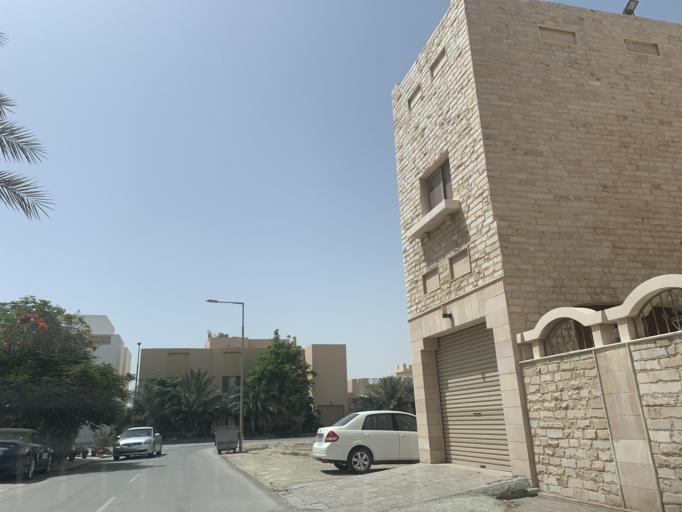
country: BH
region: Northern
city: Sitrah
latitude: 26.1566
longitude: 50.5886
